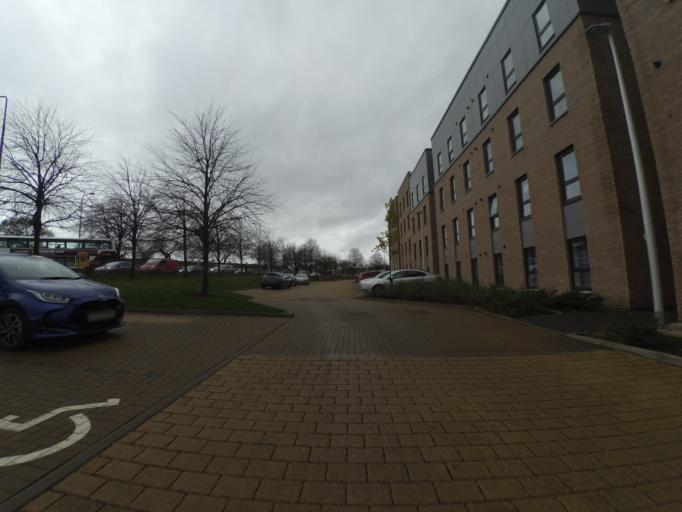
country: GB
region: Scotland
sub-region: West Lothian
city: Seafield
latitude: 55.9326
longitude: -3.1299
